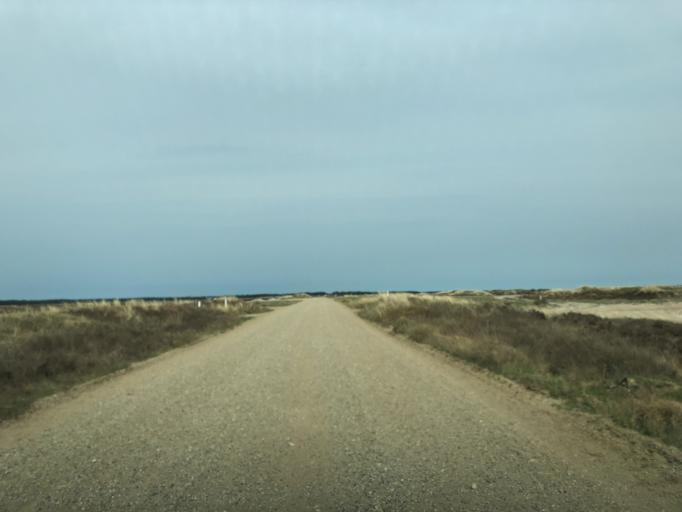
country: DK
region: South Denmark
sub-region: Varde Kommune
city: Oksbol
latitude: 55.5814
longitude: 8.1440
